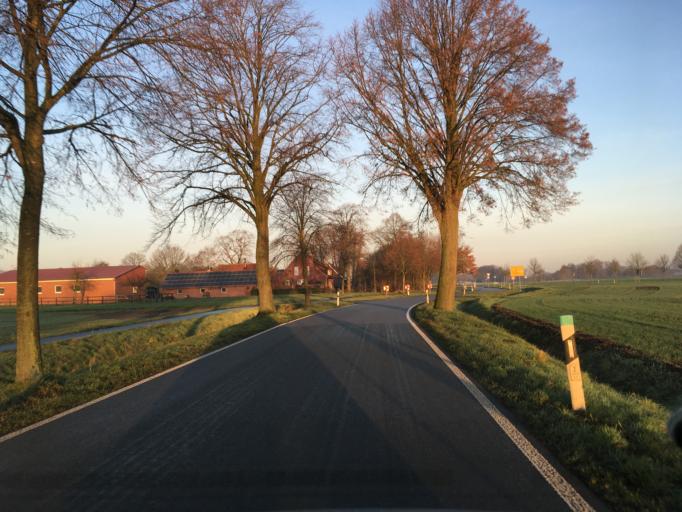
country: DE
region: North Rhine-Westphalia
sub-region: Regierungsbezirk Munster
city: Schoppingen
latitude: 52.0520
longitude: 7.2321
